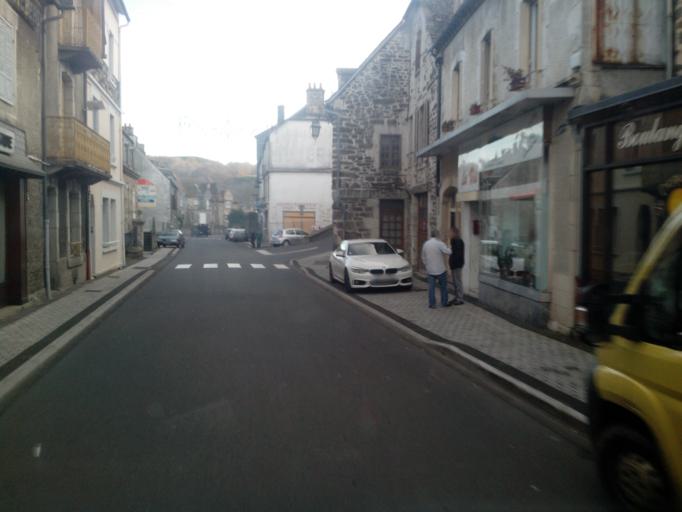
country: FR
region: Auvergne
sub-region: Departement du Cantal
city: Riom-es-Montagnes
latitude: 45.2809
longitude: 2.6600
